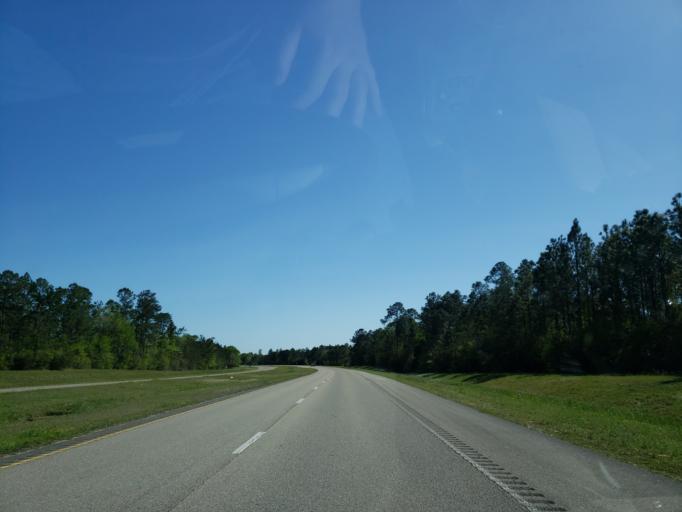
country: US
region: Mississippi
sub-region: Harrison County
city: Lyman
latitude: 30.5220
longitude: -89.0341
